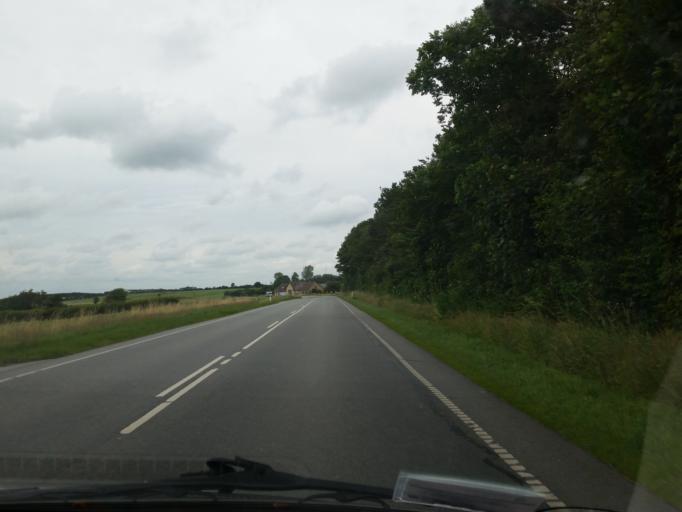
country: DK
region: South Denmark
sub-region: Vejen Kommune
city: Holsted
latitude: 55.4022
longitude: 8.9286
